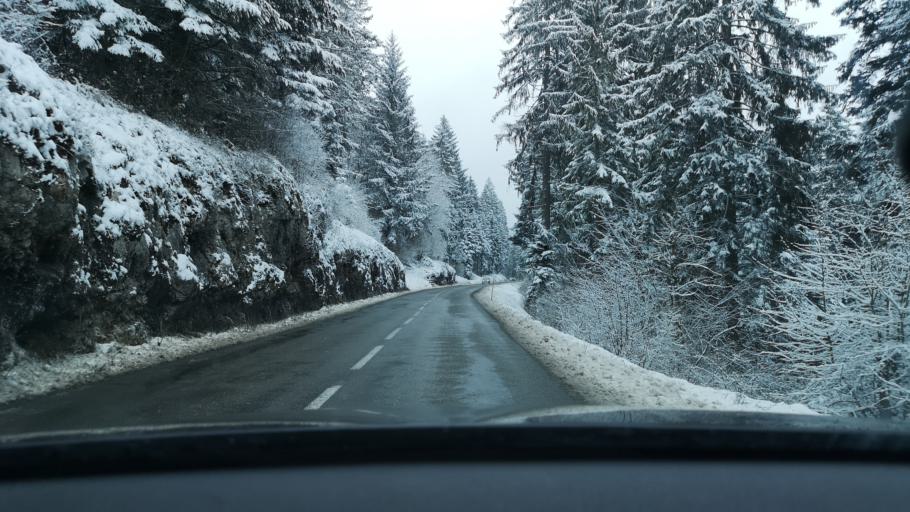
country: FR
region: Rhone-Alpes
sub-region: Departement de l'Ain
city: Oyonnax
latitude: 46.2548
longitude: 5.6701
